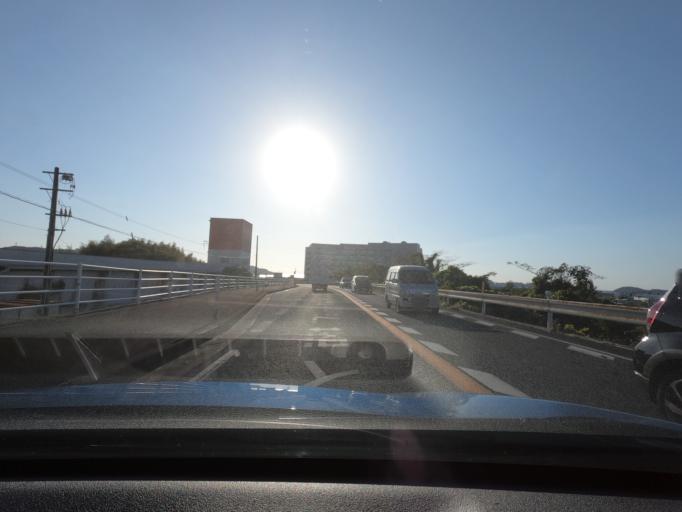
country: JP
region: Kagoshima
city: Akune
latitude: 32.0287
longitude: 130.1969
